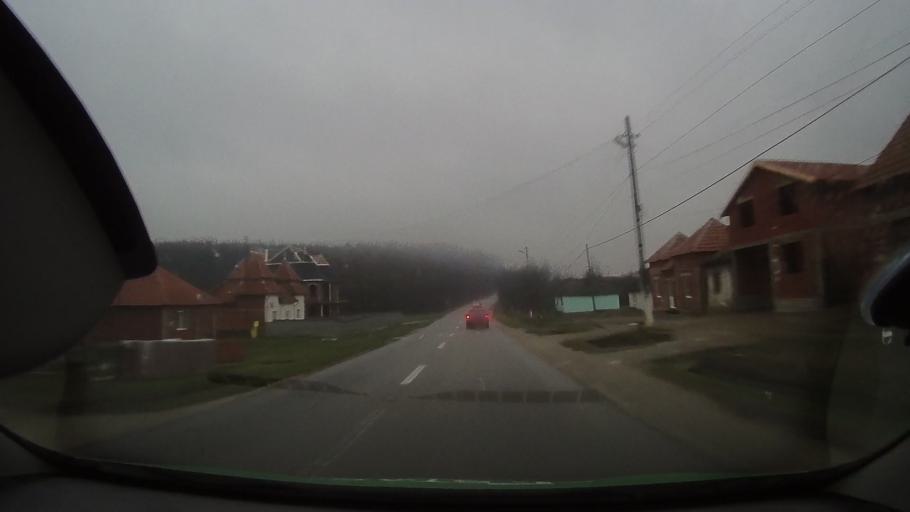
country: RO
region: Arad
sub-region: Comuna Craiova
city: Craiova
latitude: 46.5714
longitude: 21.9729
